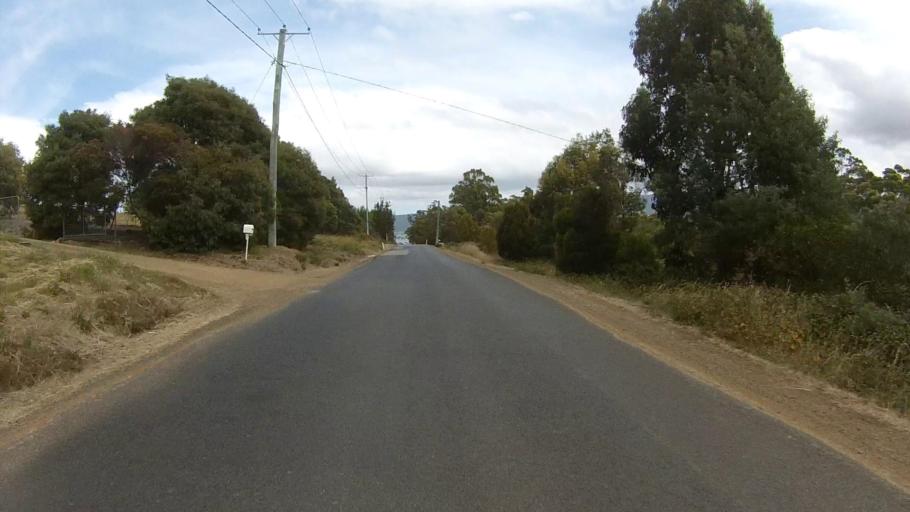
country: AU
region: Tasmania
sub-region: Kingborough
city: Blackmans Bay
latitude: -43.0311
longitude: 147.3112
